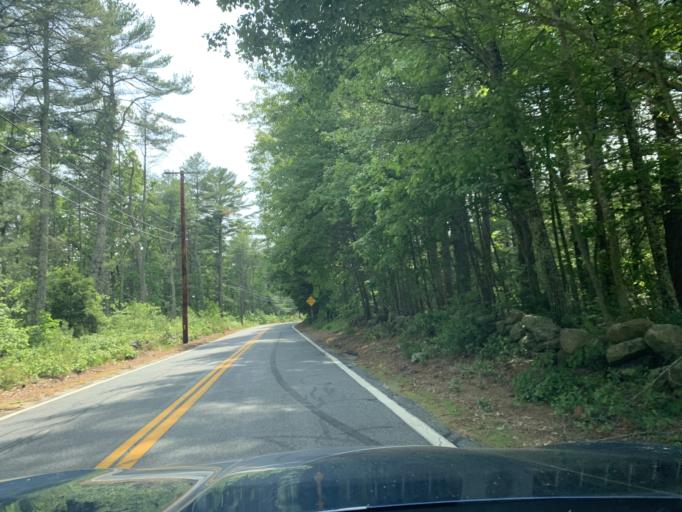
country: US
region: Rhode Island
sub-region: Kent County
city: Coventry
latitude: 41.6971
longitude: -71.7528
